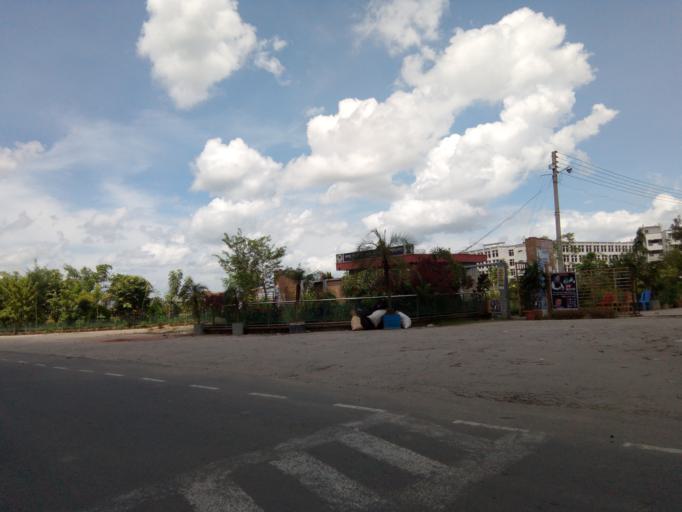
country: BD
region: Dhaka
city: Tungipara
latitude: 22.9653
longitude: 89.8158
